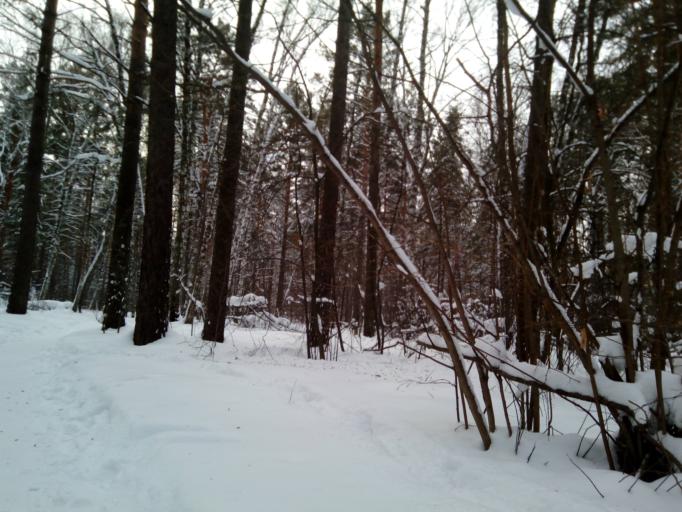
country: RU
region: Novosibirsk
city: Akademgorodok
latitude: 54.8586
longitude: 83.0929
